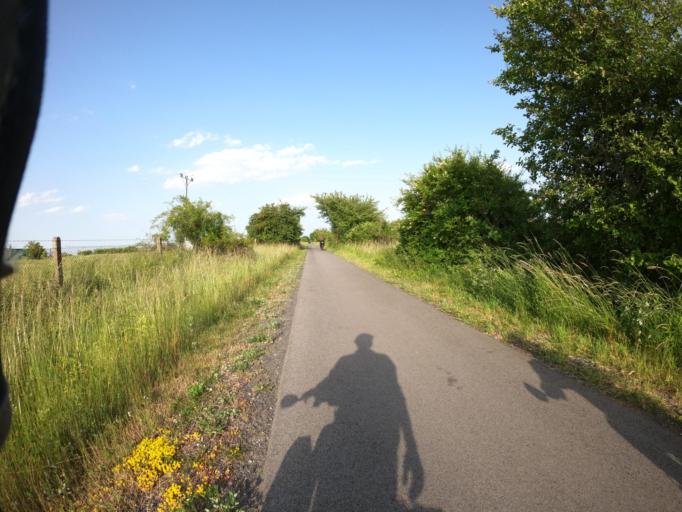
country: PL
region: West Pomeranian Voivodeship
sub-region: Powiat mysliborski
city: Barlinek
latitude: 52.9911
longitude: 15.1776
